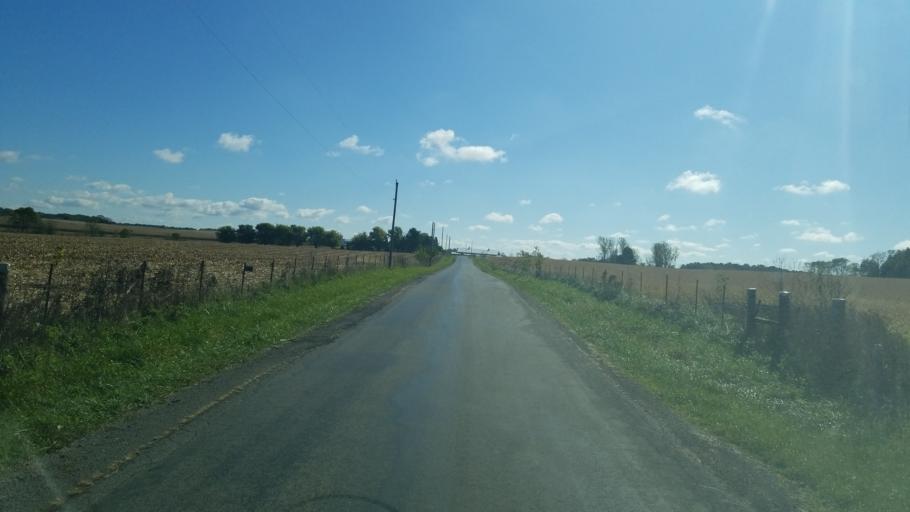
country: US
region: Ohio
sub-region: Highland County
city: Leesburg
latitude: 39.2793
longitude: -83.5706
